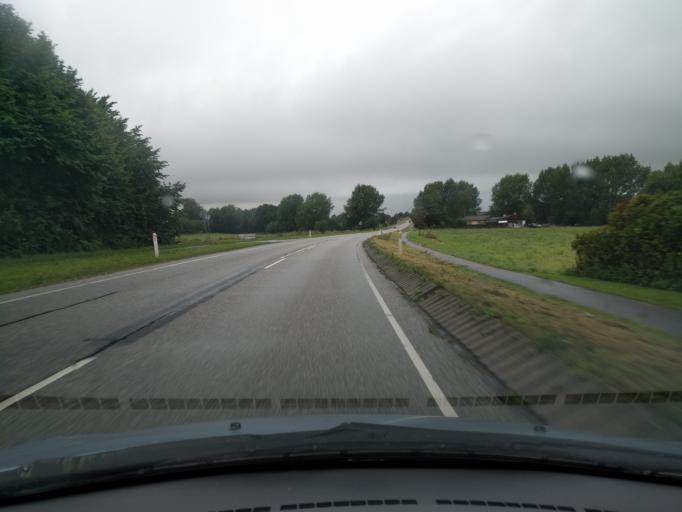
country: DK
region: Zealand
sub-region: Naestved Kommune
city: Naestved
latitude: 55.1810
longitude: 11.7836
